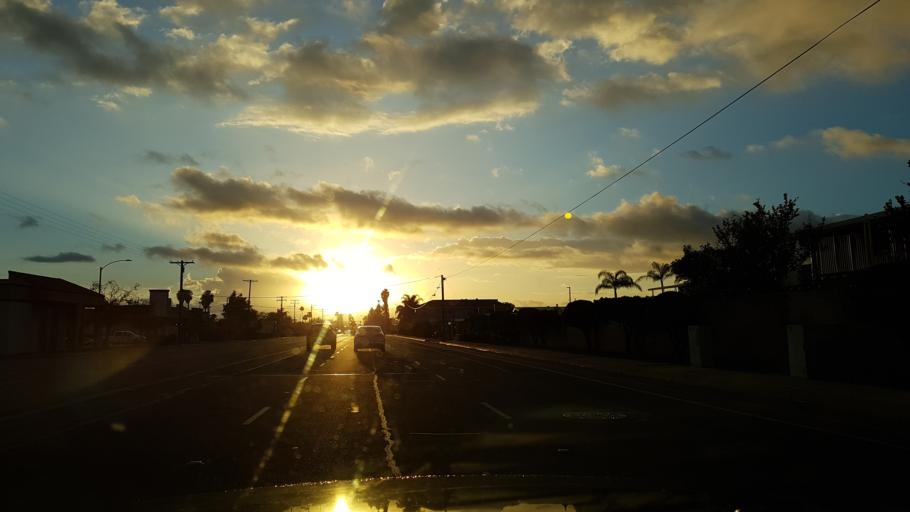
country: US
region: California
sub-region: San Diego County
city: Escondido
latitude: 33.1394
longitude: -117.0478
